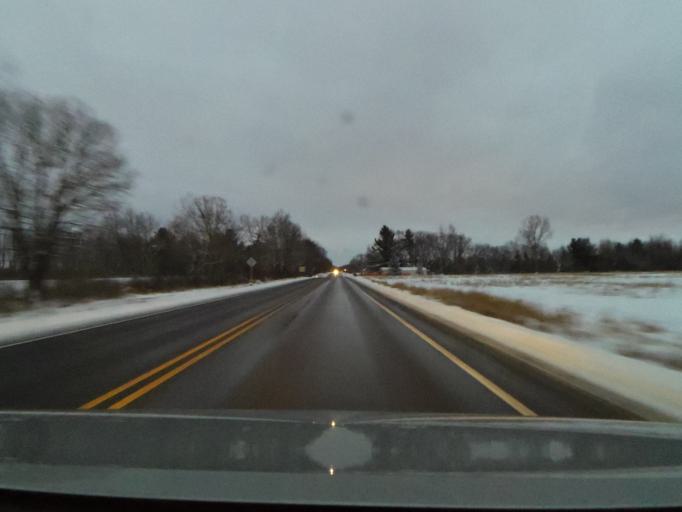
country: US
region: Wisconsin
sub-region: Dunn County
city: Menomonie
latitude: 44.9243
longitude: -91.9736
